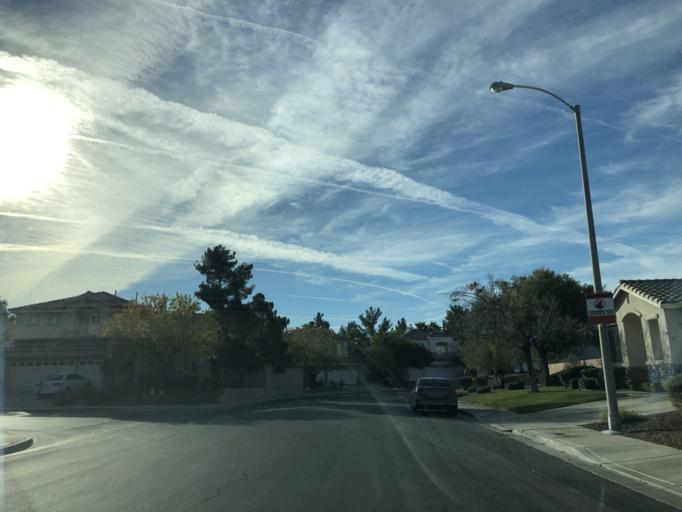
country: US
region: Nevada
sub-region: Clark County
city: Whitney
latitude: 36.0229
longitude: -115.0724
